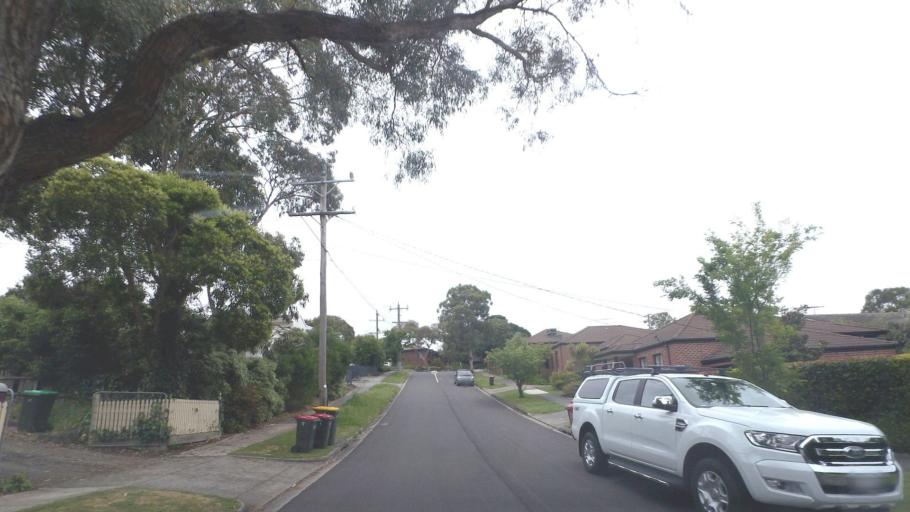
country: AU
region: Victoria
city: Mitcham
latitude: -37.8044
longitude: 145.1965
